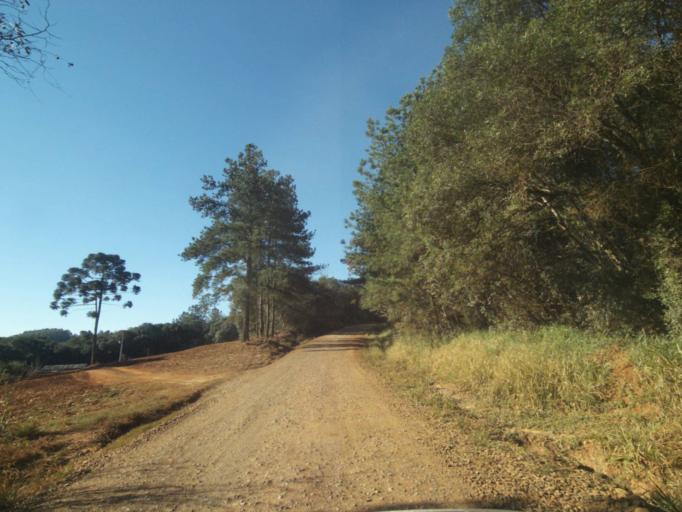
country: BR
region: Parana
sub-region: Tibagi
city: Tibagi
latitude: -24.5311
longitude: -50.4929
